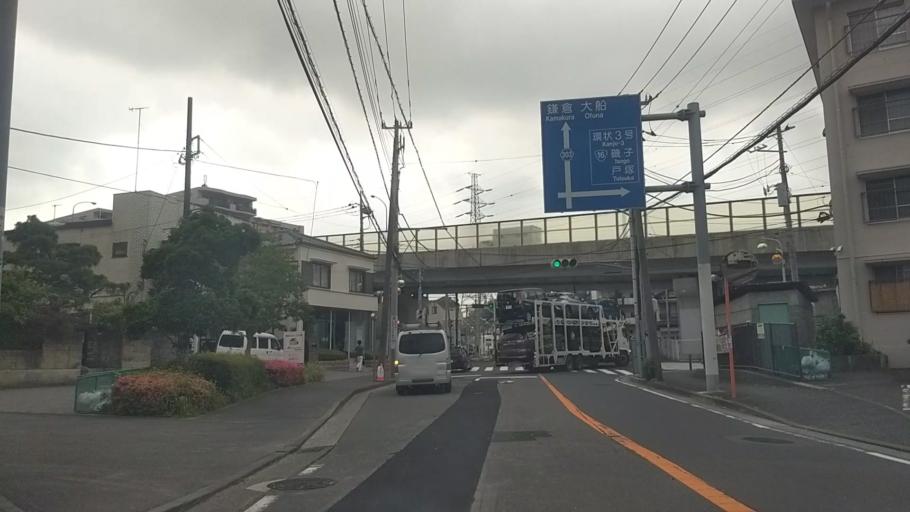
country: JP
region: Kanagawa
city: Kamakura
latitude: 35.3802
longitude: 139.5375
